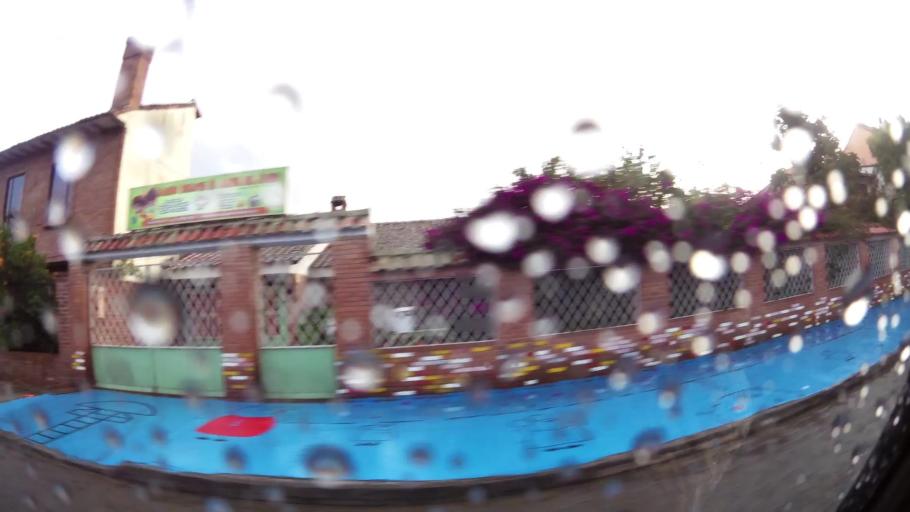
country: CO
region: Cundinamarca
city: Chia
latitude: 4.8590
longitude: -74.0566
